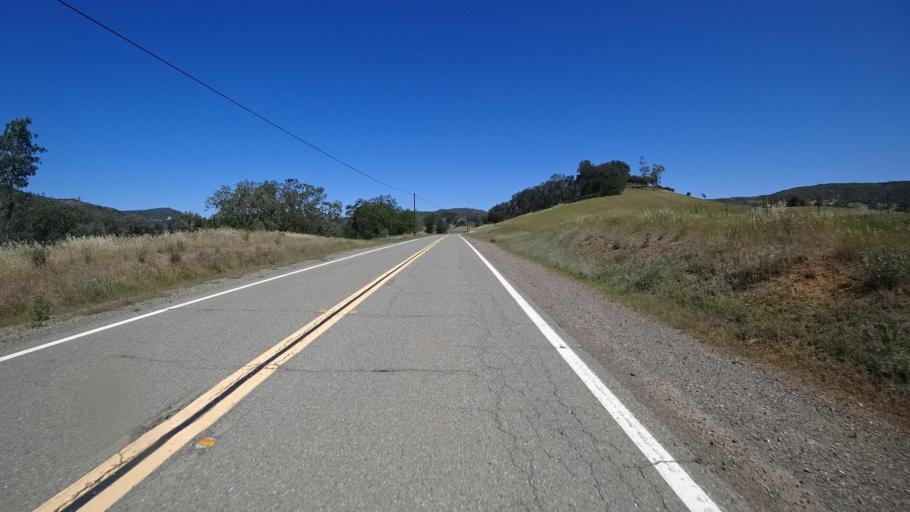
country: US
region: California
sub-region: Lake County
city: Hidden Valley Lake
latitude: 38.8669
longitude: -122.4152
